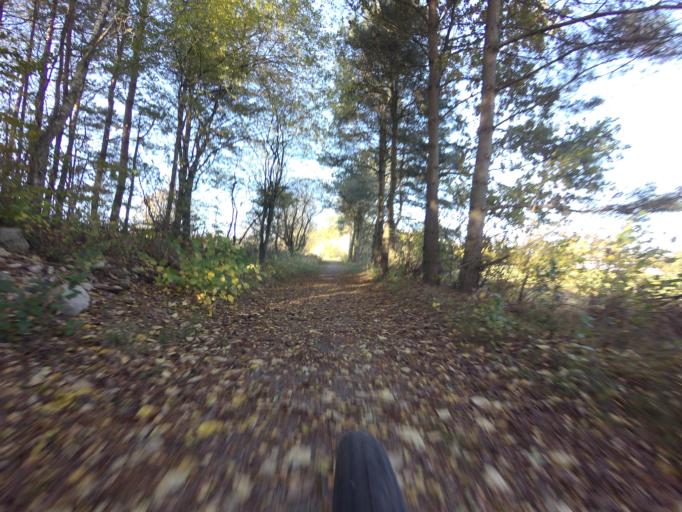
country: DK
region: Central Jutland
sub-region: Syddjurs Kommune
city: Ryomgard
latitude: 56.4819
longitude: 10.6416
